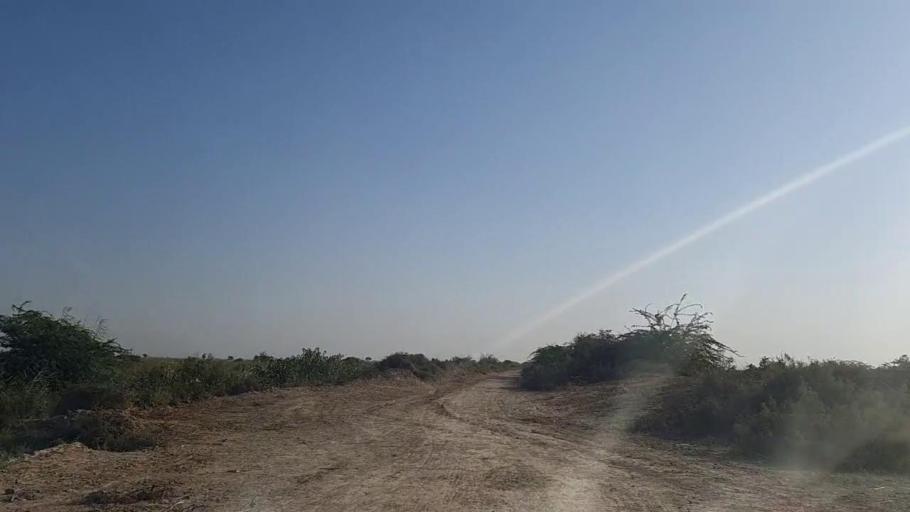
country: PK
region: Sindh
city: Jati
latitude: 24.3959
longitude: 68.2301
